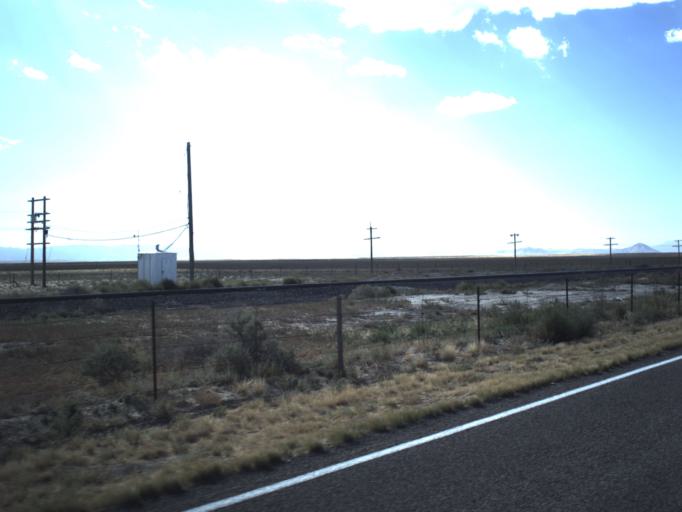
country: US
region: Utah
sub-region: Millard County
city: Delta
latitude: 39.0152
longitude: -112.7815
